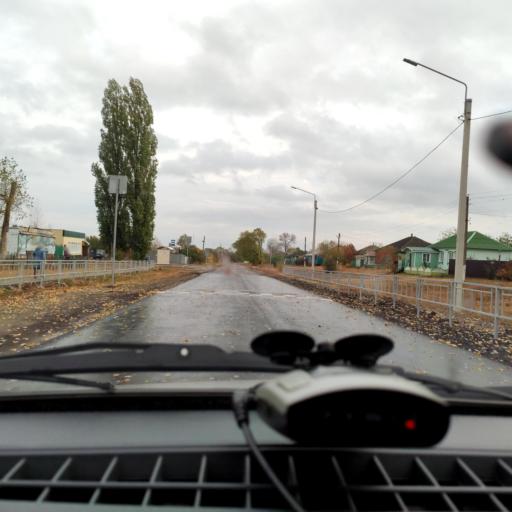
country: RU
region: Voronezj
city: Kolodeznyy
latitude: 51.2387
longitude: 39.0285
